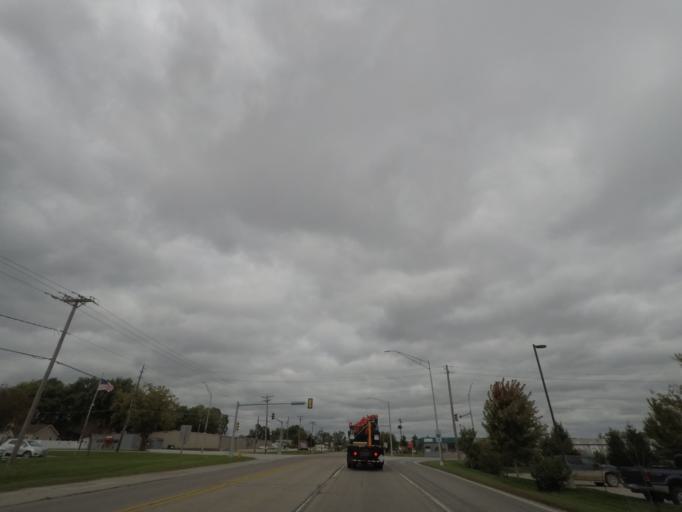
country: US
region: Iowa
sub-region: Polk County
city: Saylorville
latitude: 41.6580
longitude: -93.6005
